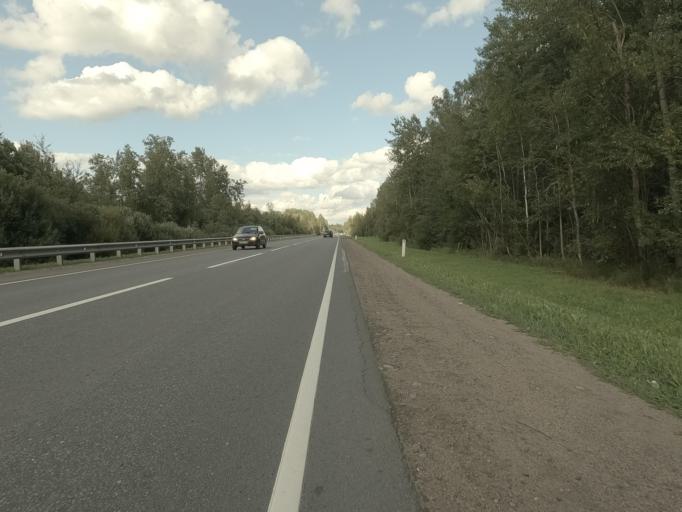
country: RU
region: Leningrad
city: Nikol'skoye
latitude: 59.6589
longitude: 30.8685
